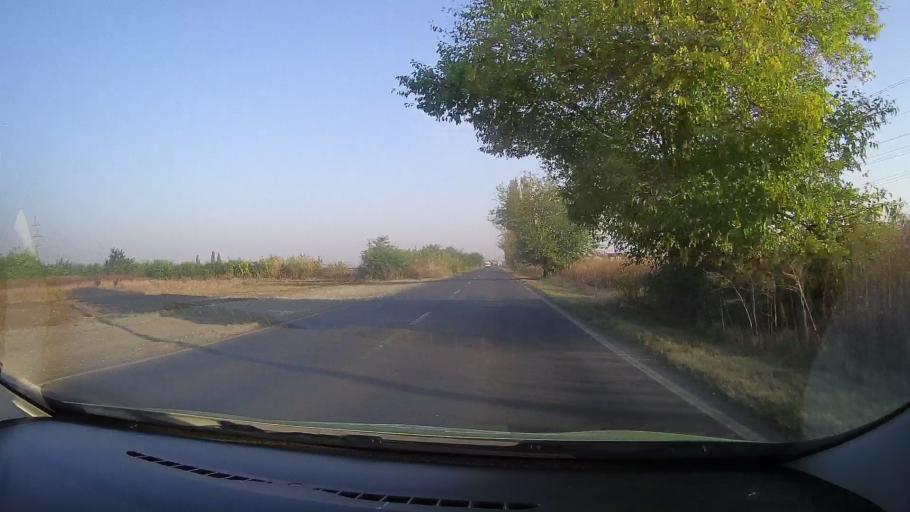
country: RO
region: Arad
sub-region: Comuna Curtici
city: Curtici
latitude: 46.3245
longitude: 21.3059
